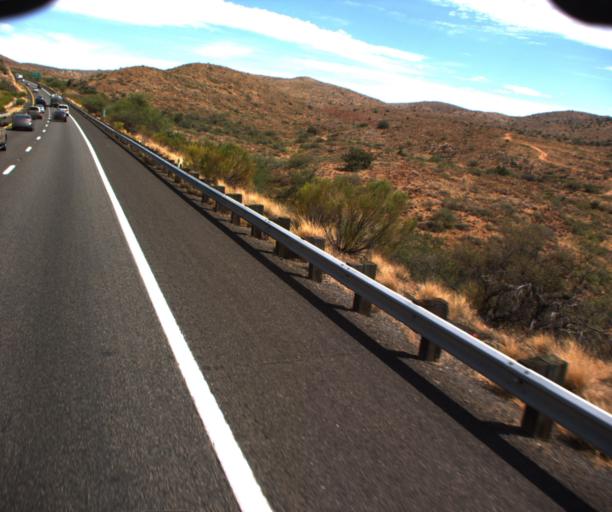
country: US
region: Arizona
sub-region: Yavapai County
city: Cordes Lakes
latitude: 34.2643
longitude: -112.1110
